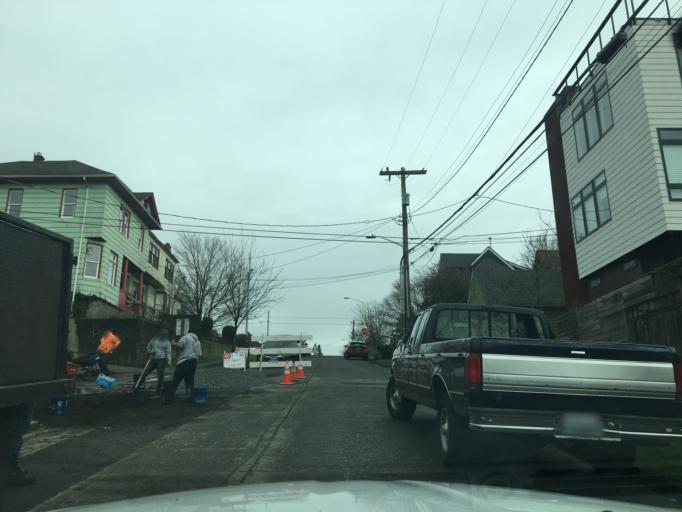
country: US
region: Washington
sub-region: King County
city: Seattle
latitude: 47.6026
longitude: -122.3035
